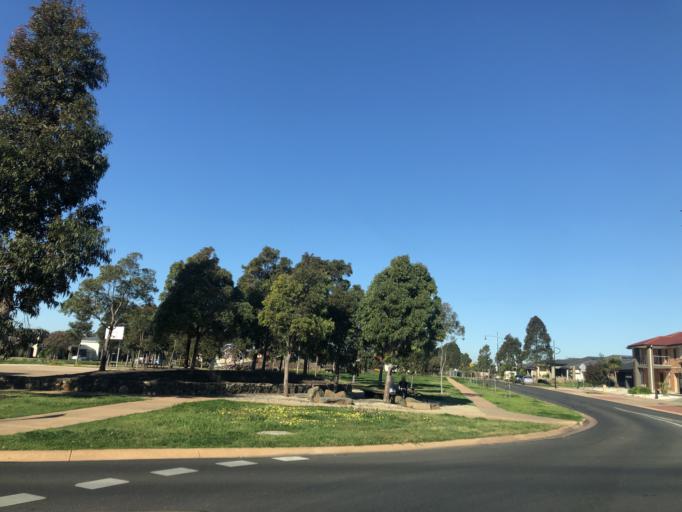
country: AU
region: Victoria
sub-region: Wyndham
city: Hoppers Crossing
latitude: -37.8948
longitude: 144.7209
